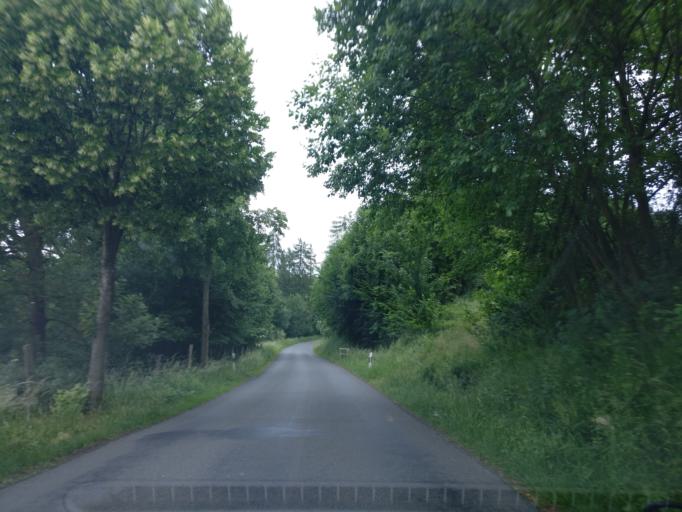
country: DE
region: Lower Saxony
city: Scheden
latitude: 51.4187
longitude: 9.7186
